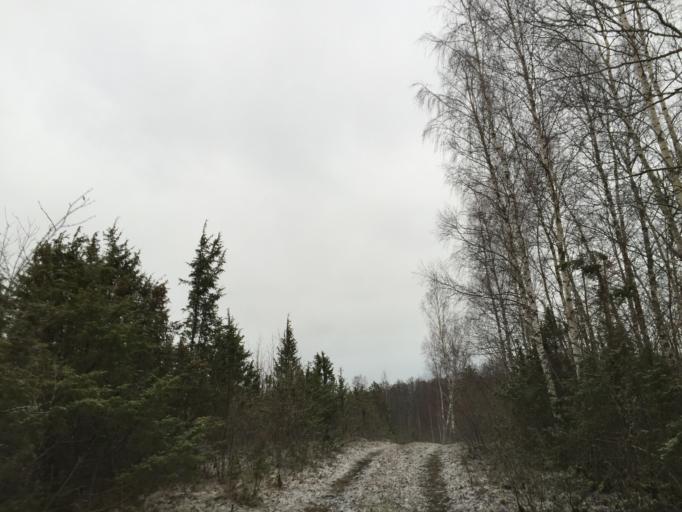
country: EE
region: Saare
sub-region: Orissaare vald
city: Orissaare
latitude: 58.6678
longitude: 23.2405
